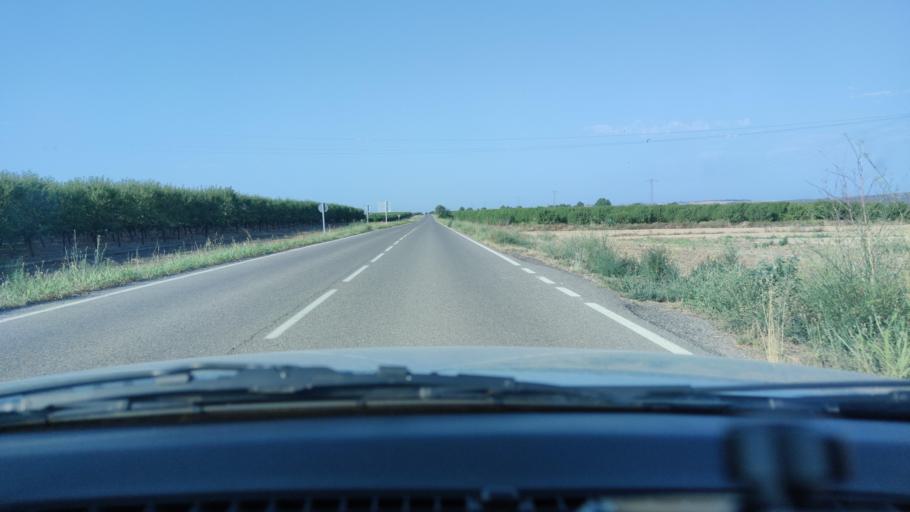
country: ES
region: Catalonia
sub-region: Provincia de Lleida
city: Balaguer
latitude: 41.8199
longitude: 0.8389
